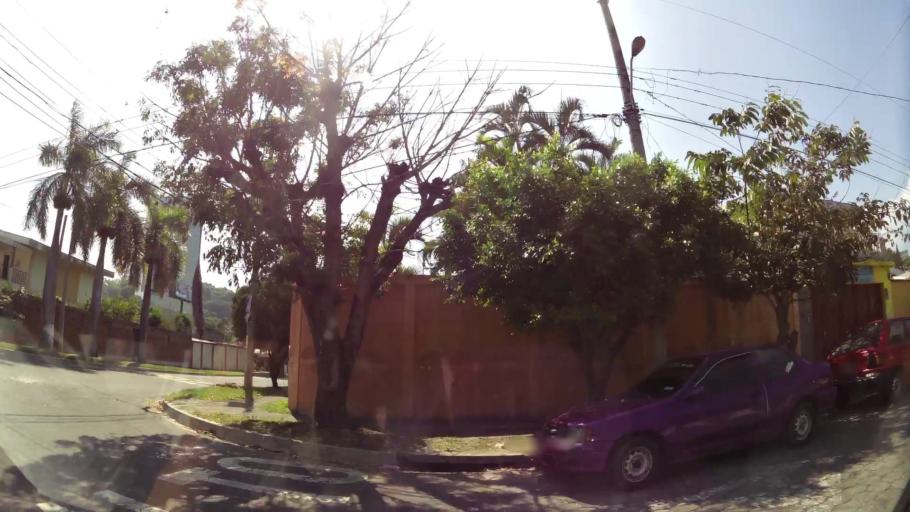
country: SV
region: La Libertad
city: Antiguo Cuscatlan
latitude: 13.6844
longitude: -89.2333
